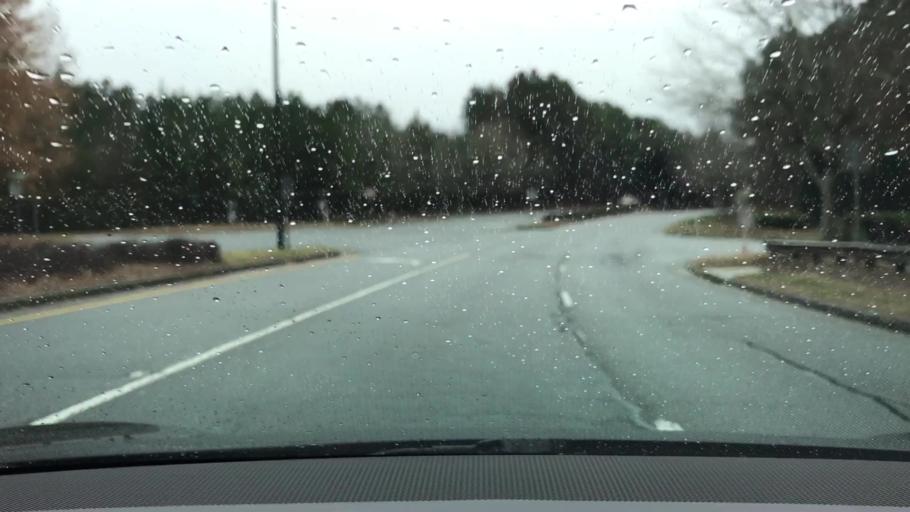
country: US
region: Georgia
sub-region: Gwinnett County
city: Suwanee
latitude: 34.0223
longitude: -84.0633
